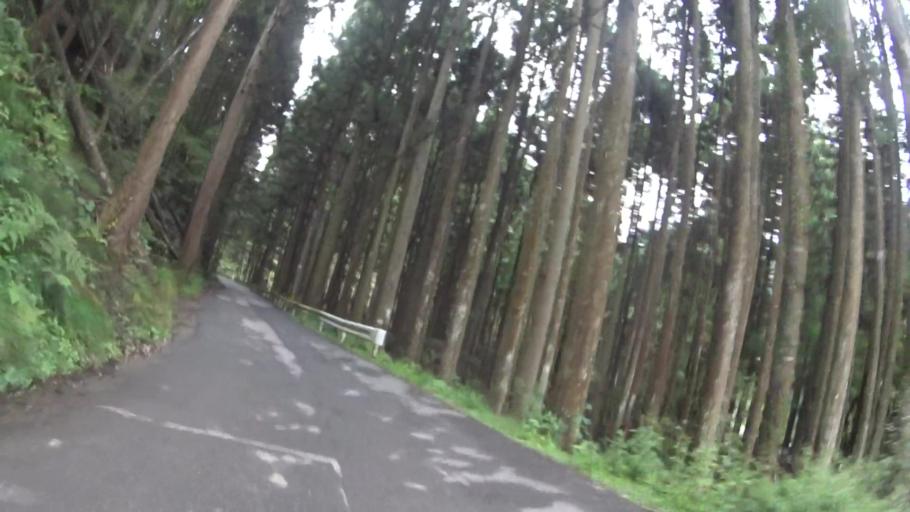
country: JP
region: Kyoto
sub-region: Kyoto-shi
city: Kamigyo-ku
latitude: 35.1279
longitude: 135.7792
